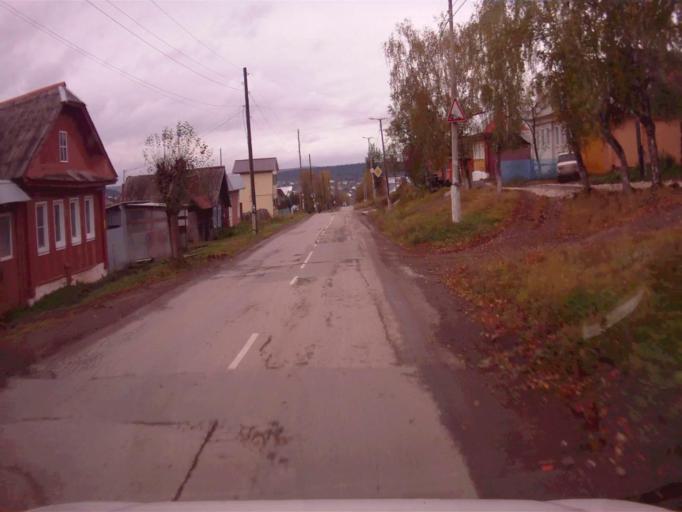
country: RU
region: Chelyabinsk
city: Nyazepetrovsk
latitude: 56.0593
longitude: 59.6106
